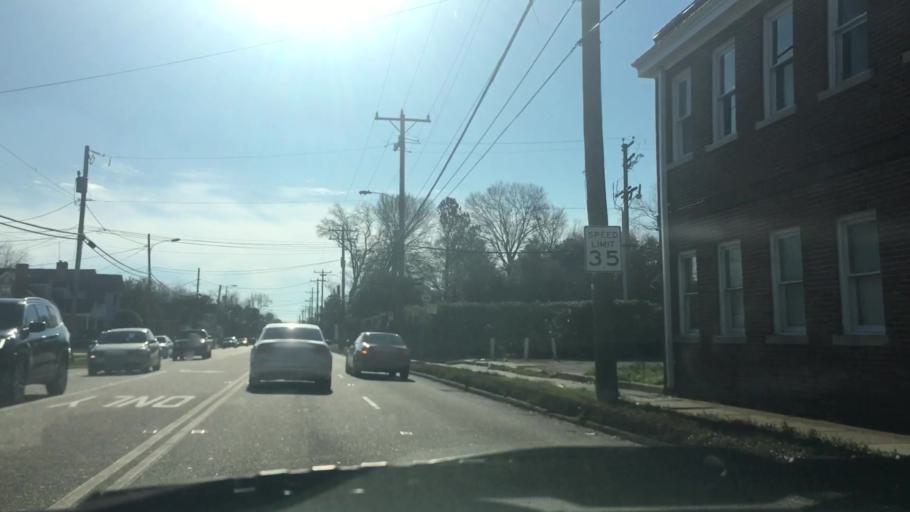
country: US
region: Virginia
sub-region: City of Norfolk
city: Norfolk
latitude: 36.8774
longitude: -76.2637
